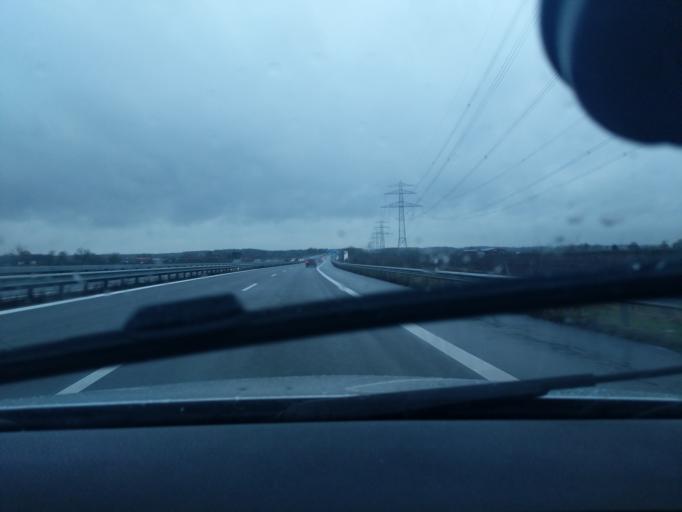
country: DE
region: Lower Saxony
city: Neuenkirchen
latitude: 53.5120
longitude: 9.6069
